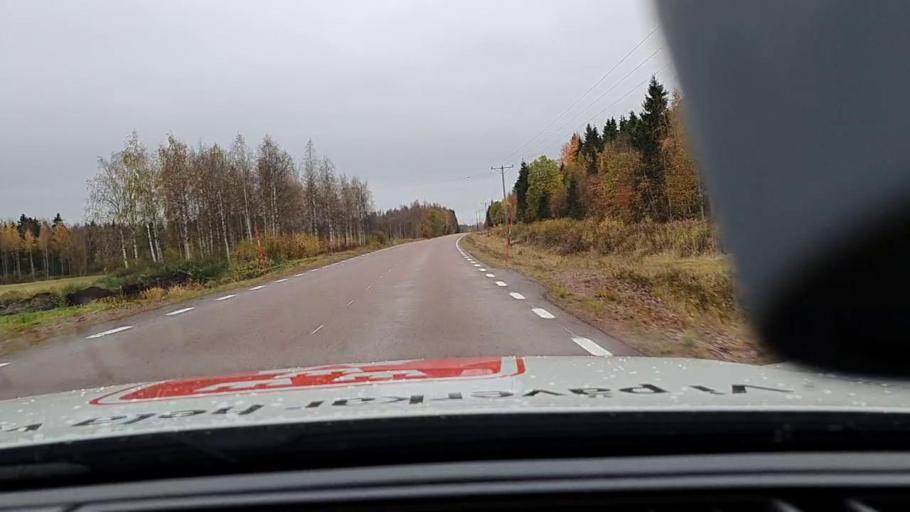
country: FI
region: Lapland
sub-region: Torniolaakso
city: Ylitornio
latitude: 66.1278
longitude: 23.9106
